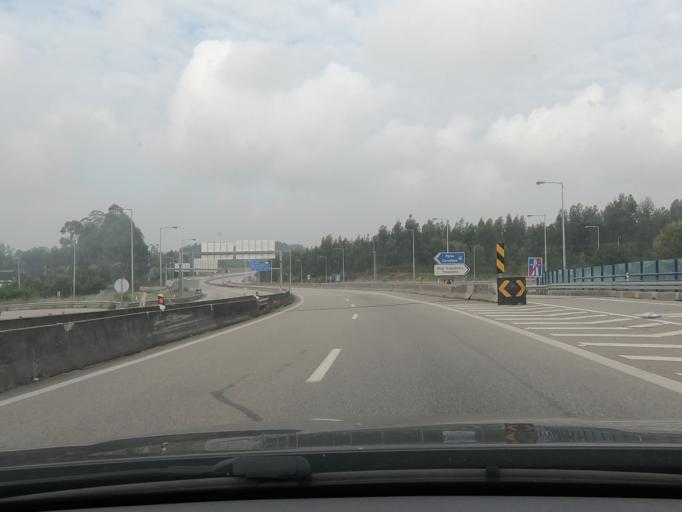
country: PT
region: Porto
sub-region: Vila Nova de Gaia
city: Grijo
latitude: 41.0119
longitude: -8.5738
